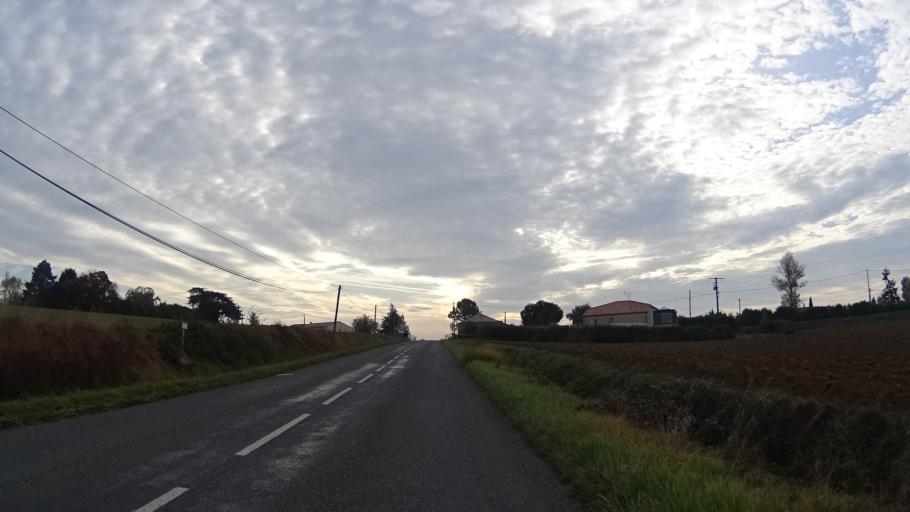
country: FR
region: Aquitaine
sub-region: Departement du Lot-et-Garonne
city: Laplume
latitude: 44.0992
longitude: 0.5605
